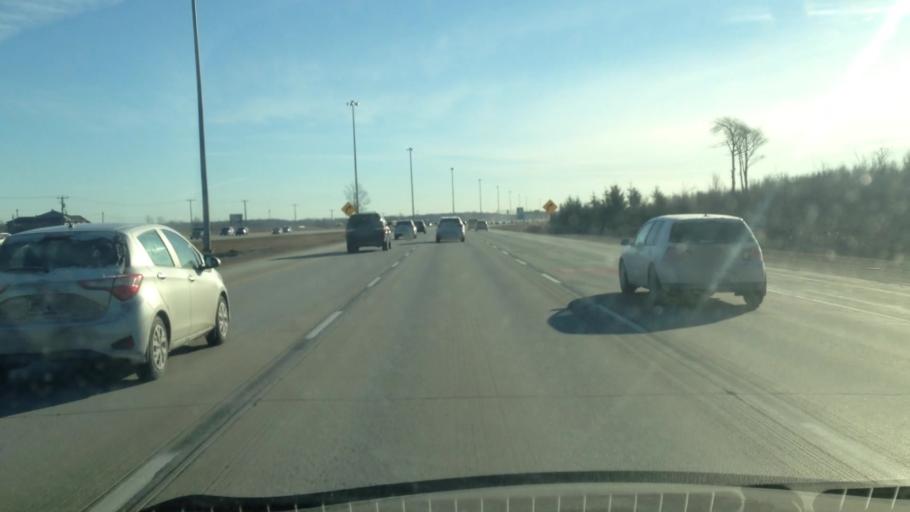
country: CA
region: Quebec
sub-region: Laurentides
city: Saint-Jerome
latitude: 45.7353
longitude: -73.9857
